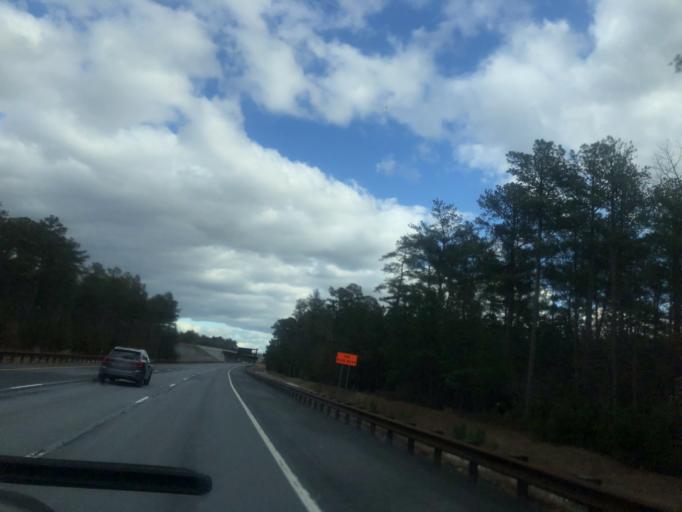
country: US
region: New Jersey
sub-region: Ocean County
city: Tuckerton
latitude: 39.6160
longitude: -74.4166
